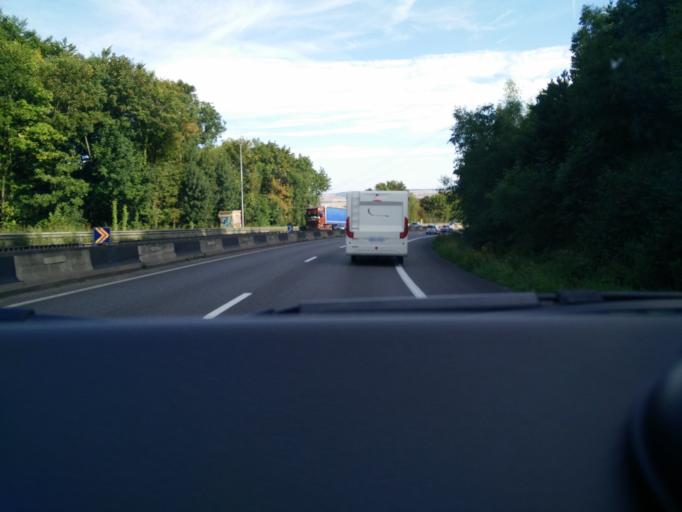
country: FR
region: Lorraine
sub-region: Departement de Meurthe-et-Moselle
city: Vandoeuvre-les-Nancy
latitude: 48.6410
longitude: 6.1697
